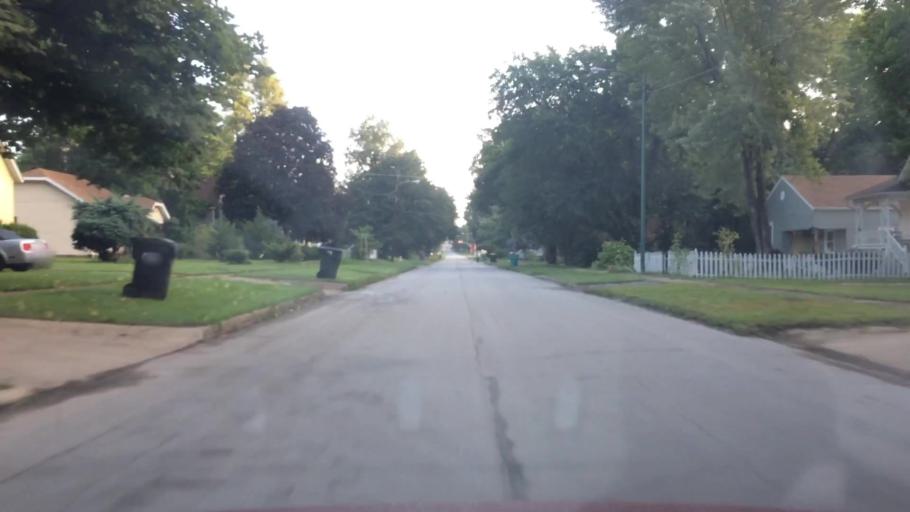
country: US
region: Missouri
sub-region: Greene County
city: Springfield
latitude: 37.2221
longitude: -93.2809
